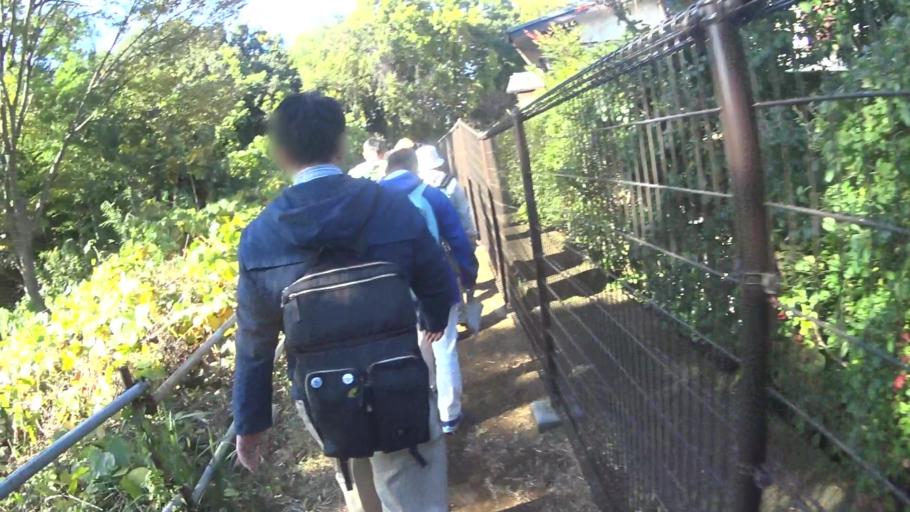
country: JP
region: Tokyo
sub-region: Machida-shi
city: Machida
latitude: 35.6055
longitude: 139.4891
